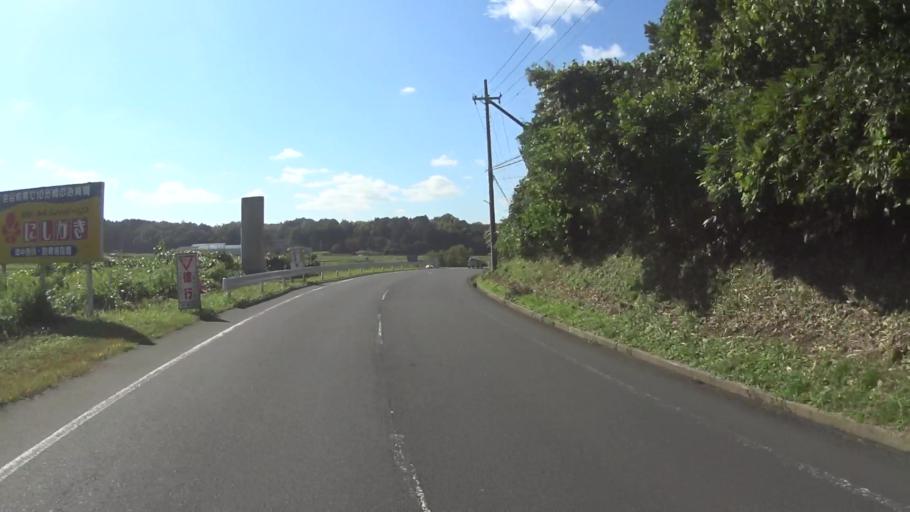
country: JP
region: Kyoto
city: Miyazu
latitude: 35.6445
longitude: 135.0844
